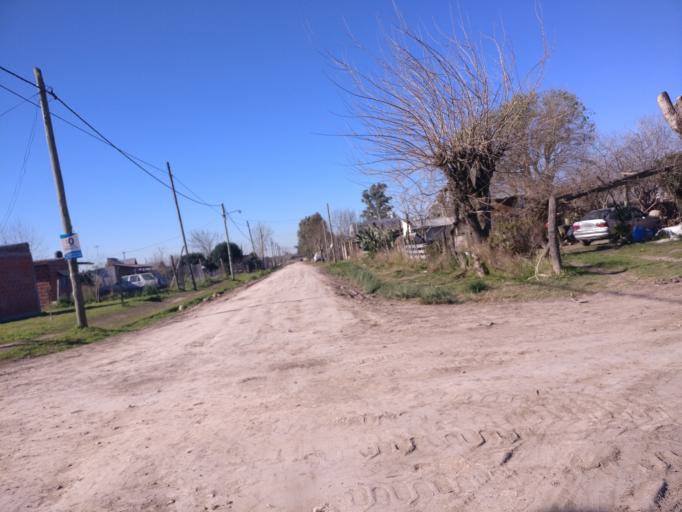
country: AR
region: Buenos Aires
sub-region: Partido de Ezeiza
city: Ezeiza
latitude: -34.9404
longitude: -58.6054
